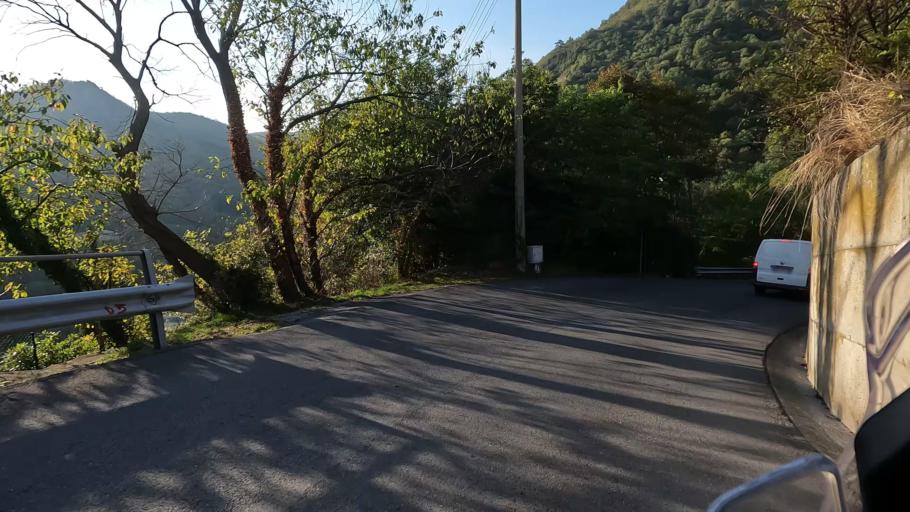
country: IT
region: Liguria
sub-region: Provincia di Savona
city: San Giovanni
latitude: 44.4030
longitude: 8.5333
